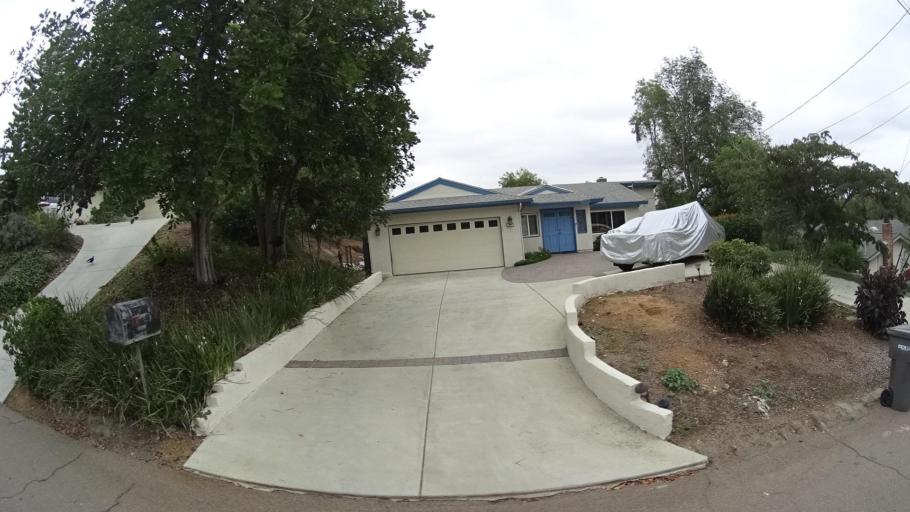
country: US
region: California
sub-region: San Diego County
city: Casa de Oro-Mount Helix
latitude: 32.7603
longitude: -116.9735
